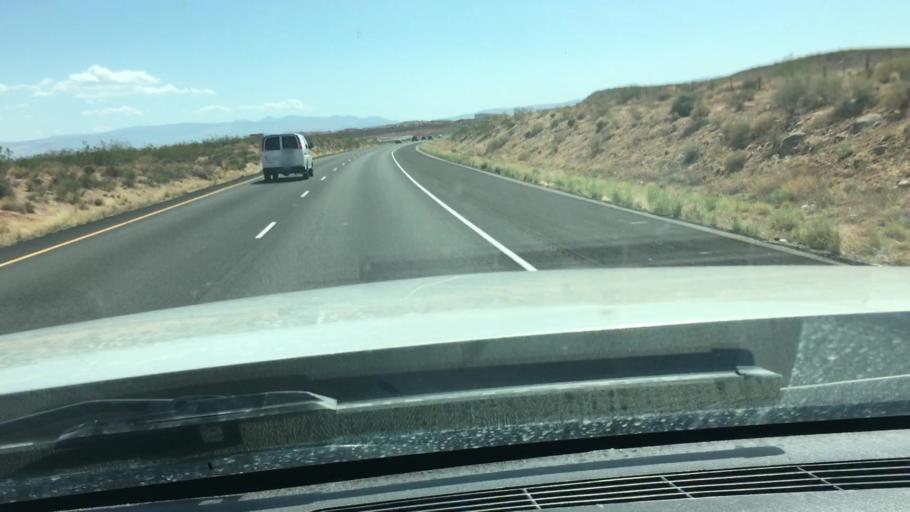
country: US
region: Utah
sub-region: Washington County
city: Washington
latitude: 37.1813
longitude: -113.4171
